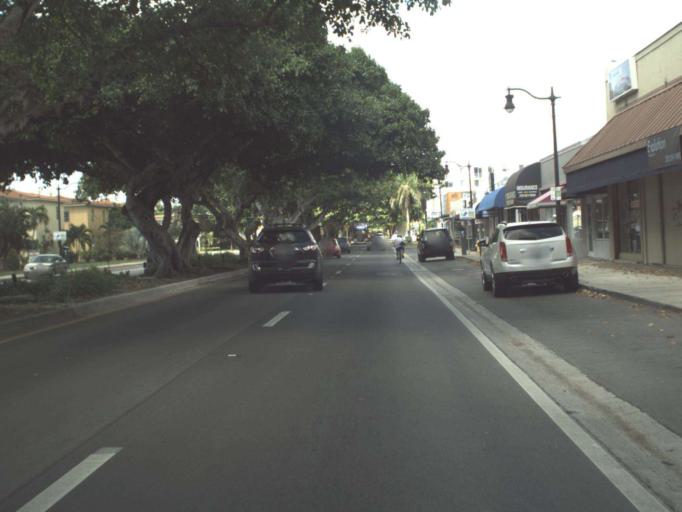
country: US
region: Florida
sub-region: Miami-Dade County
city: Coconut Grove
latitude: 25.7506
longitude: -80.2327
